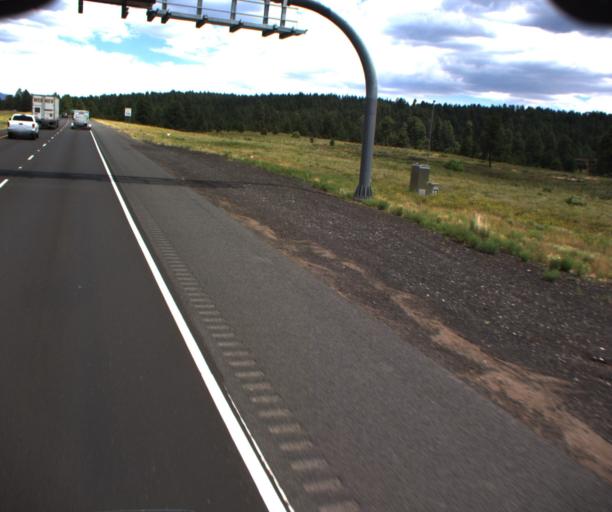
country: US
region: Arizona
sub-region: Coconino County
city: Kachina Village
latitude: 35.1009
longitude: -111.6821
